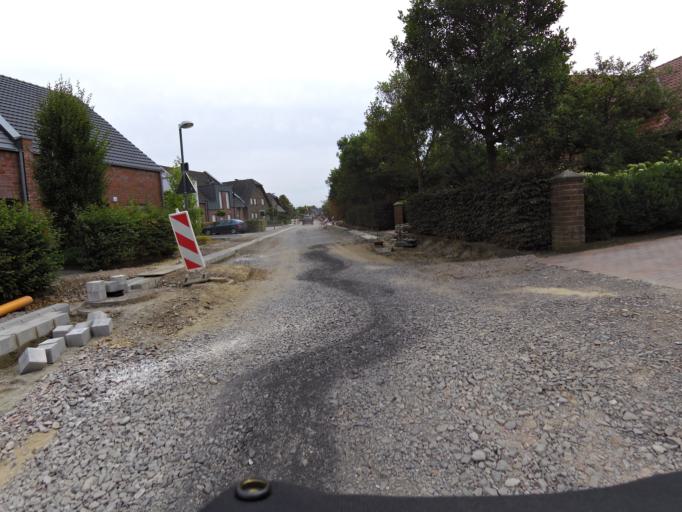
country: DE
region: North Rhine-Westphalia
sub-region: Regierungsbezirk Dusseldorf
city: Kevelaer
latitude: 51.5828
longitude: 6.2265
